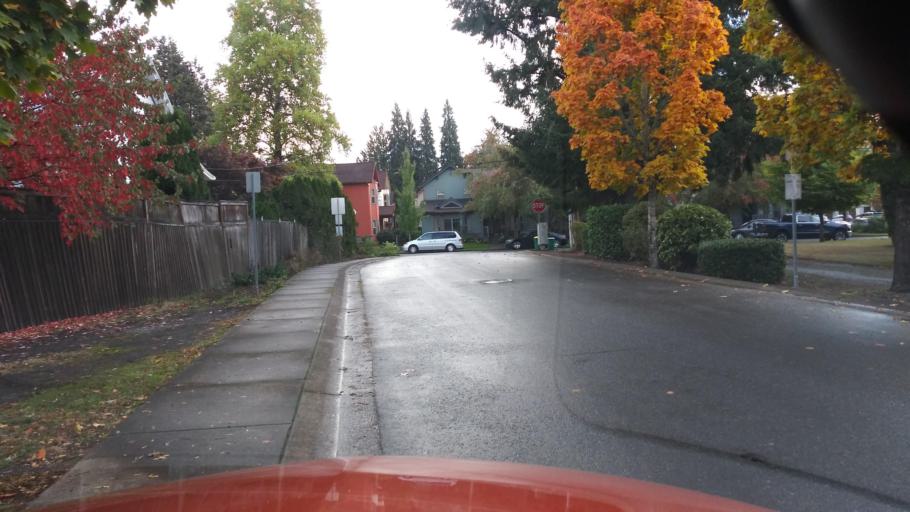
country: US
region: Oregon
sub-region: Washington County
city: Forest Grove
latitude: 45.5214
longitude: -123.1024
